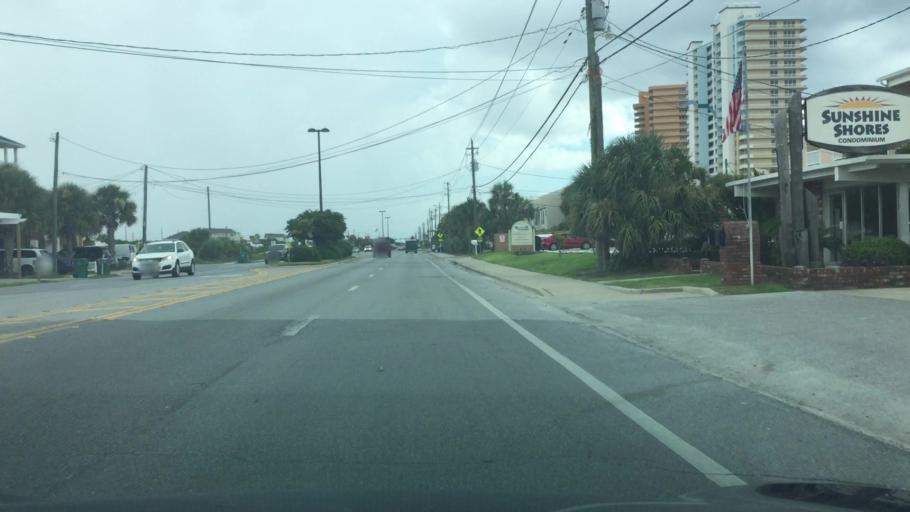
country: US
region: Florida
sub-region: Bay County
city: Lower Grand Lagoon
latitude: 30.1434
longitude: -85.7556
